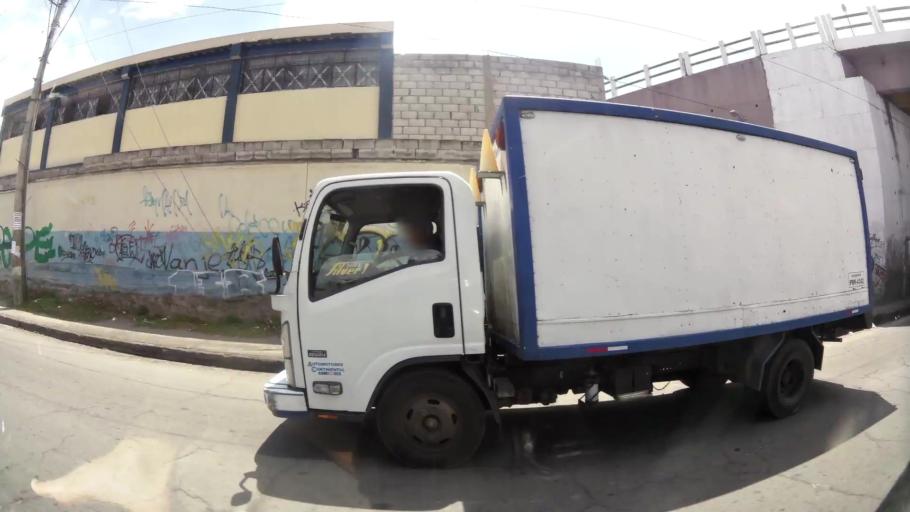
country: EC
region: Pichincha
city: Quito
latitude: -0.1045
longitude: -78.4228
